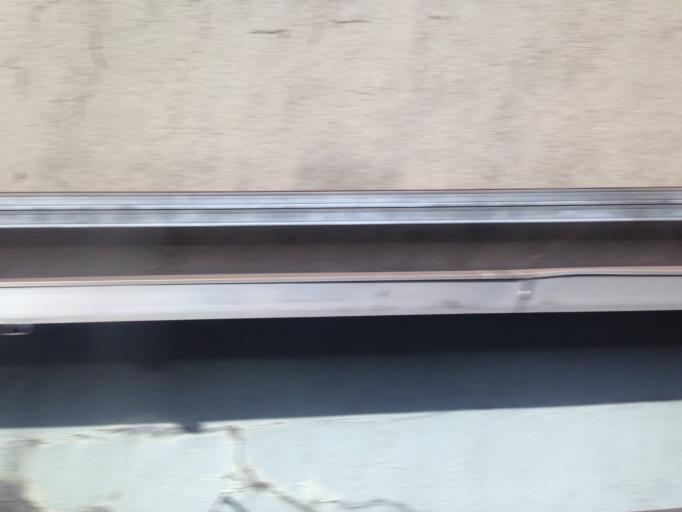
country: AU
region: New South Wales
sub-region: City of Sydney
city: Sydney
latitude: -33.8585
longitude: 151.2066
